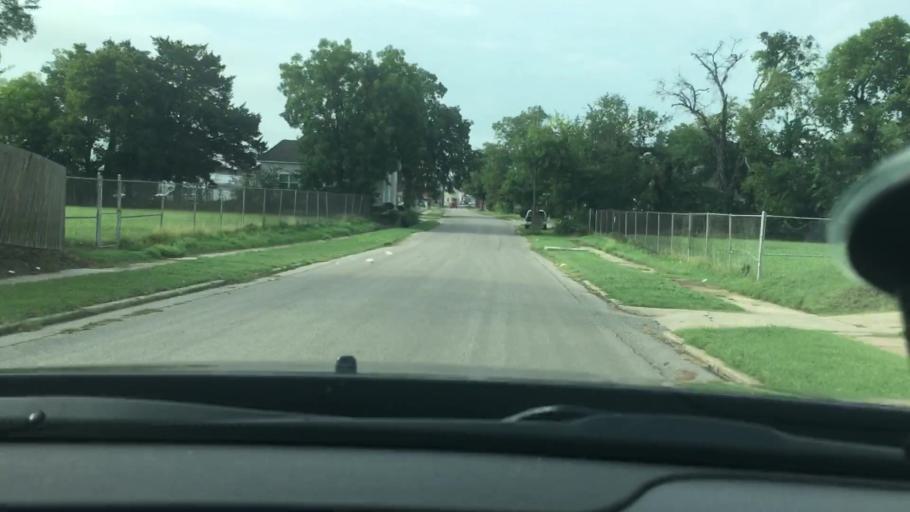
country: US
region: Oklahoma
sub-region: Carter County
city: Ardmore
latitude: 34.1776
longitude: -97.1295
